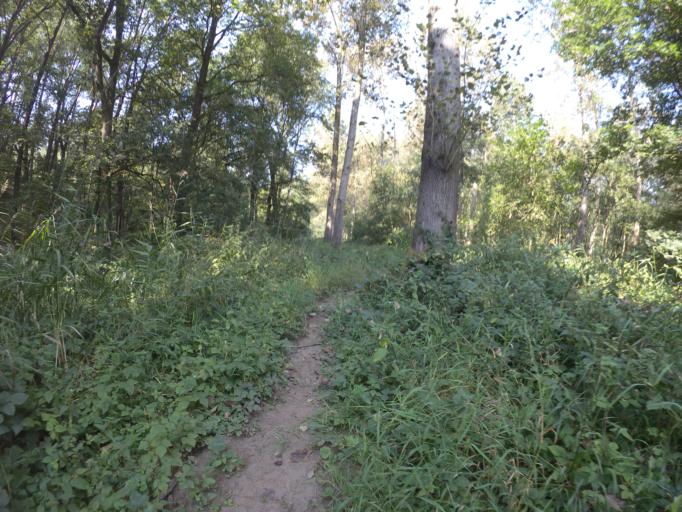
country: NL
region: North Brabant
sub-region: Gemeente Schijndel
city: Schijndel
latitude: 51.6411
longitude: 5.4525
